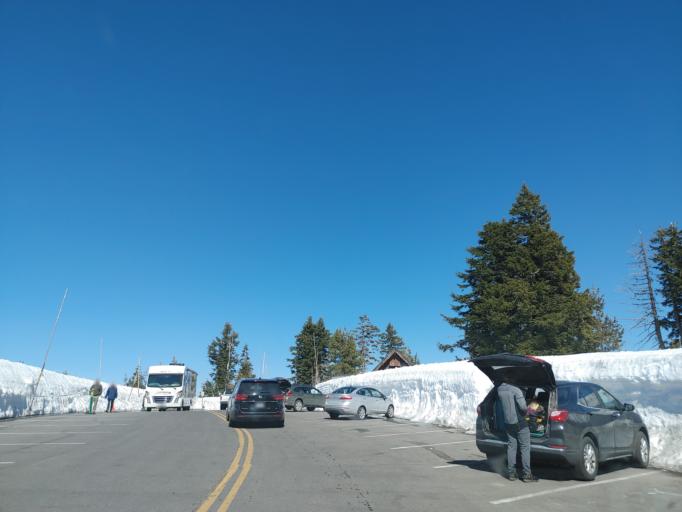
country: US
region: Oregon
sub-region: Jackson County
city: Shady Cove
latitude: 42.9109
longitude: -122.1462
